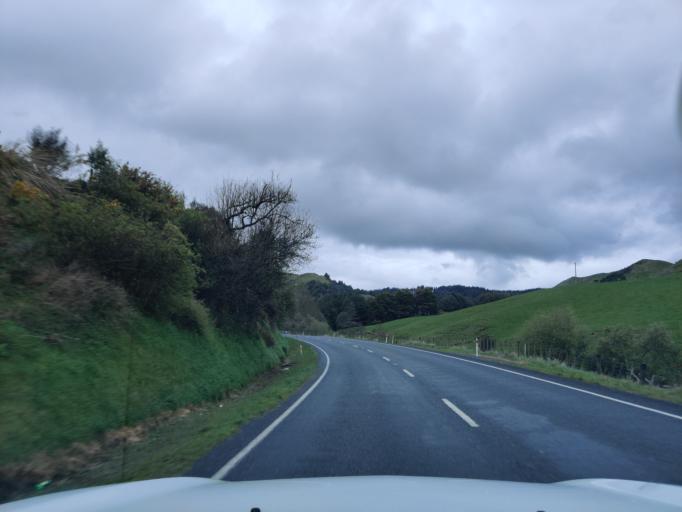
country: NZ
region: Waikato
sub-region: Otorohanga District
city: Otorohanga
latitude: -38.5194
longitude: 175.2012
